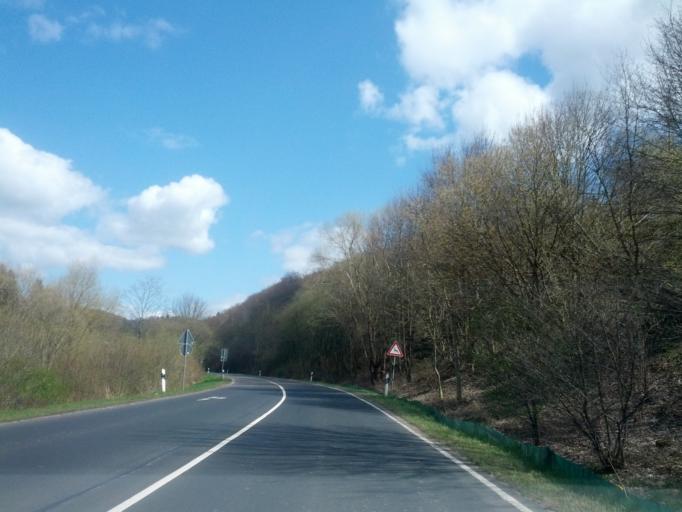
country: DE
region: Thuringia
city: Thal
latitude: 50.9148
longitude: 10.4034
